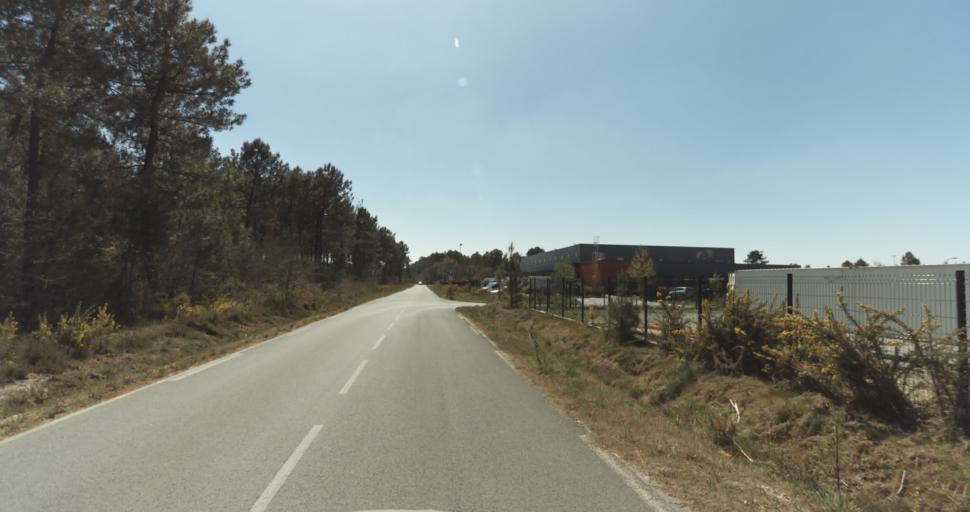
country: FR
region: Aquitaine
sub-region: Departement de la Gironde
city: Martignas-sur-Jalle
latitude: 44.8056
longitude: -0.7525
